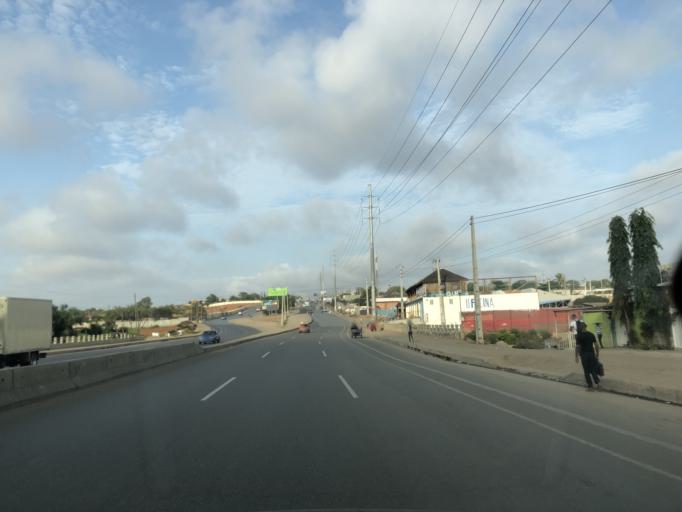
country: AO
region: Luanda
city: Luanda
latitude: -8.8970
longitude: 13.2207
